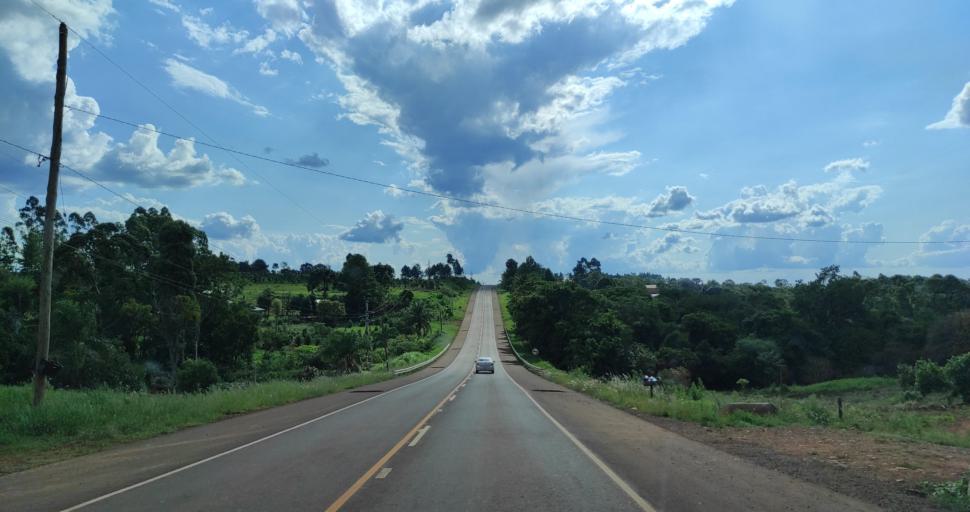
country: AR
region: Misiones
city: Bernardo de Irigoyen
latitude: -26.2940
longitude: -53.7751
